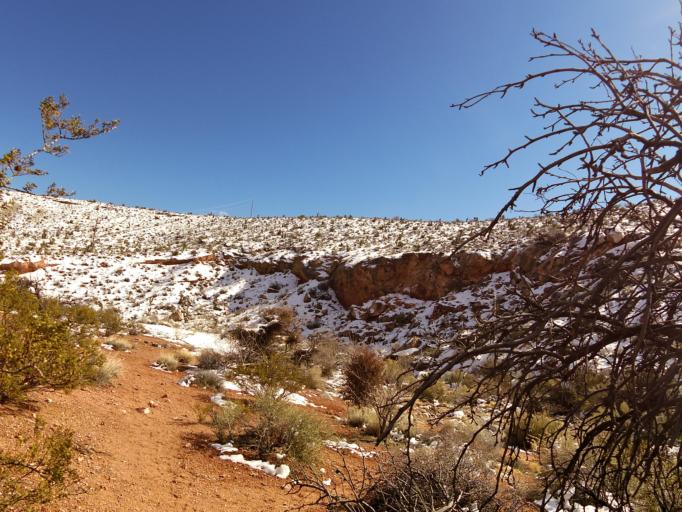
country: US
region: Nevada
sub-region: Clark County
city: Summerlin South
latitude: 36.1414
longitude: -115.4203
